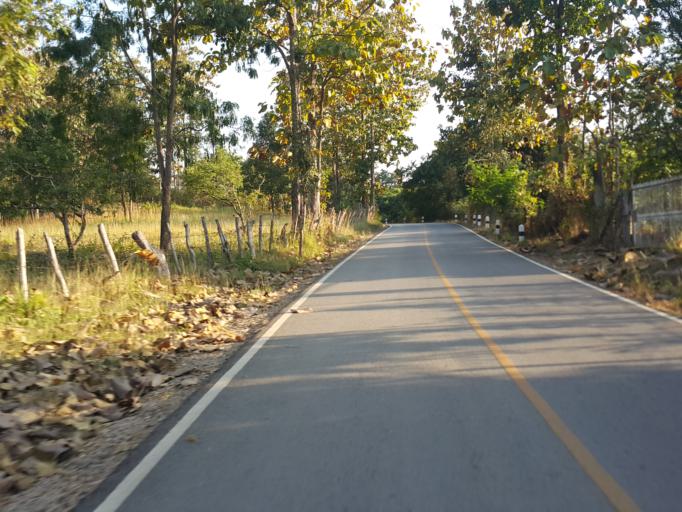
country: TH
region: Chiang Mai
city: Mae On
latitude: 18.7973
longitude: 99.2504
